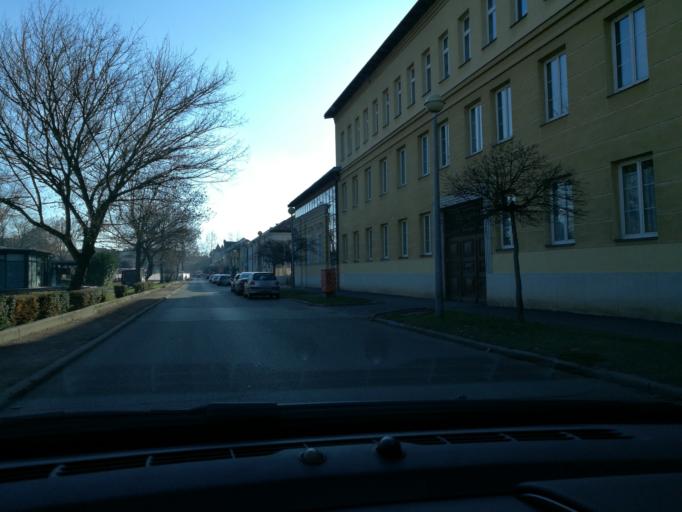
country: HU
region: Szabolcs-Szatmar-Bereg
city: Nyiregyhaza
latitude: 47.9520
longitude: 21.7128
